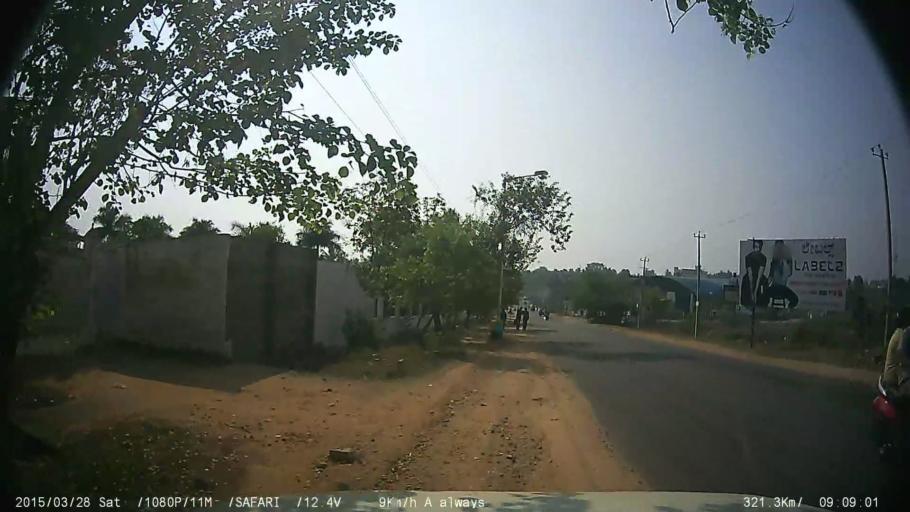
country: IN
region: Karnataka
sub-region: Mysore
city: Mysore
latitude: 12.3559
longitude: 76.6045
